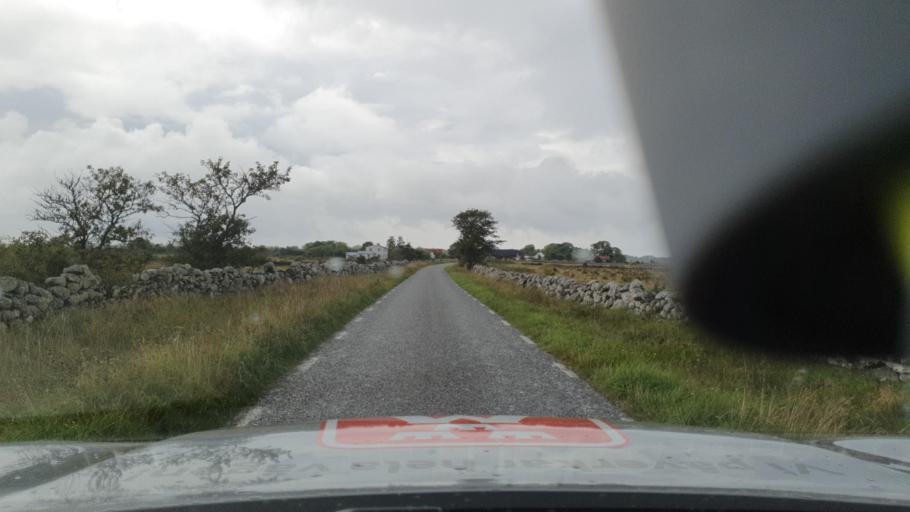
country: SE
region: Gotland
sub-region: Gotland
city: Hemse
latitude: 57.0013
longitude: 18.3552
